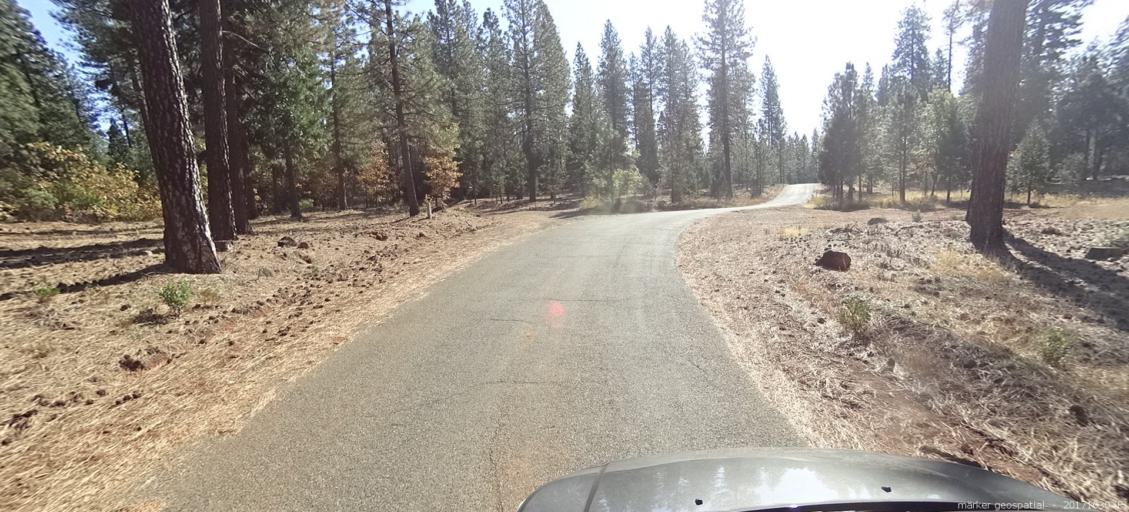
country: US
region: California
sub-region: Shasta County
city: Shingletown
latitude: 40.6035
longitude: -121.8578
